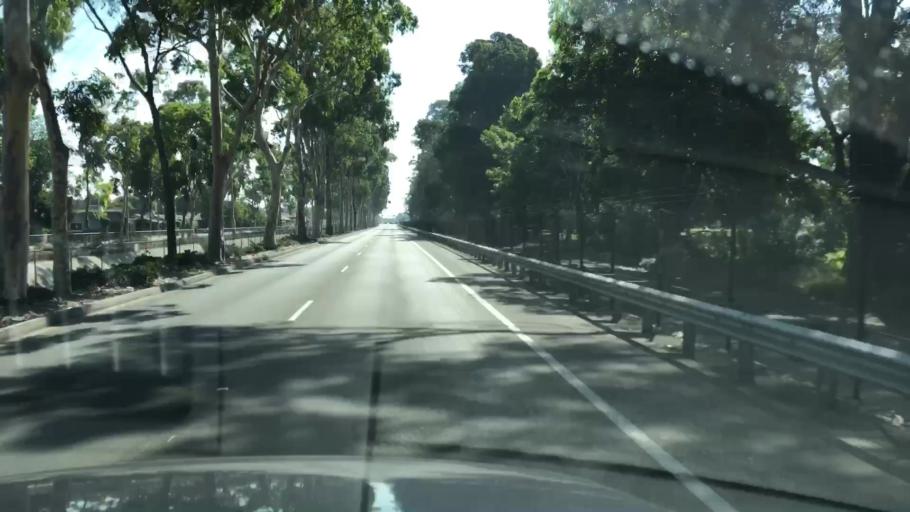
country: US
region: California
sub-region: Ventura County
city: Channel Islands Beach
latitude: 34.1757
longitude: -119.2016
